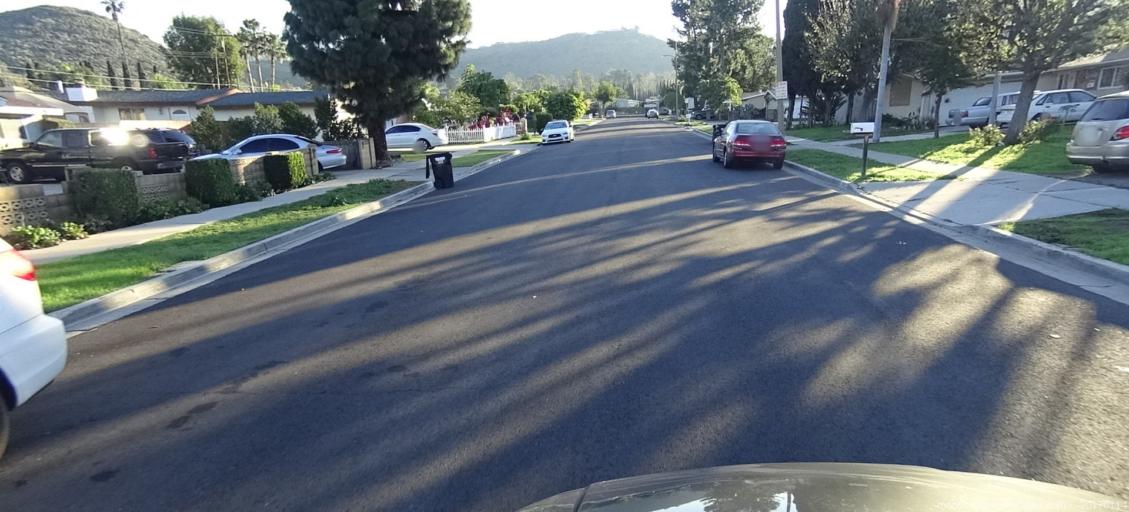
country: US
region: California
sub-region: Orange County
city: North Tustin
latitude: 33.7891
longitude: -117.8012
